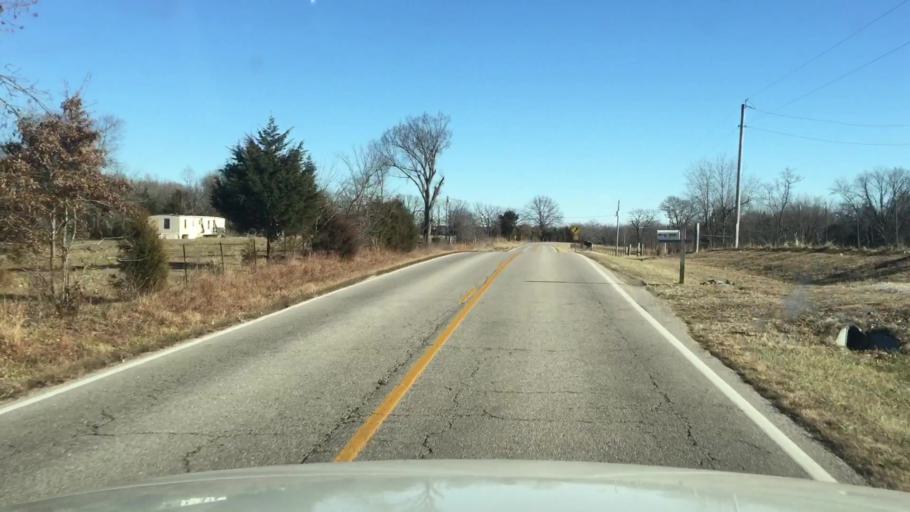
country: US
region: Missouri
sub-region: Morgan County
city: Versailles
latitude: 38.3448
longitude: -92.7357
